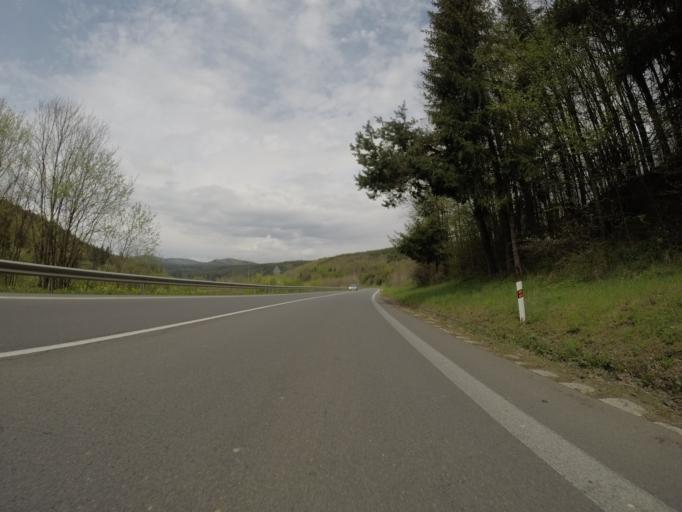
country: SK
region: Banskobystricky
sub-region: Okres Banska Bystrica
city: Brezno
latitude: 48.8192
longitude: 19.7060
